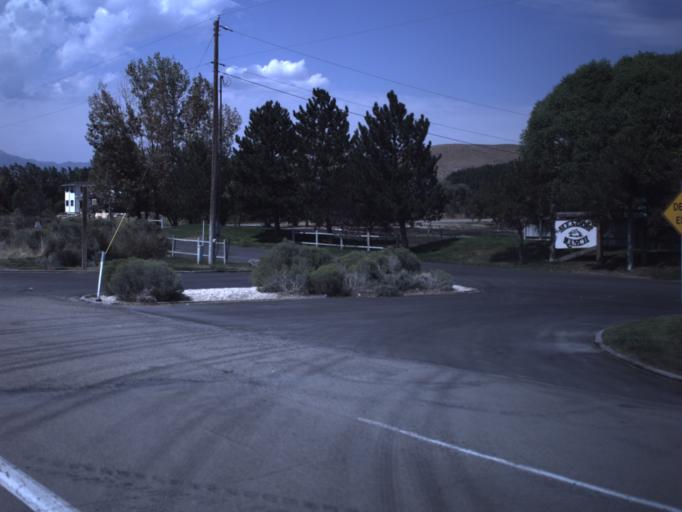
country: US
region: Utah
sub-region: Utah County
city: Eagle Mountain
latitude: 40.3804
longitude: -111.9809
